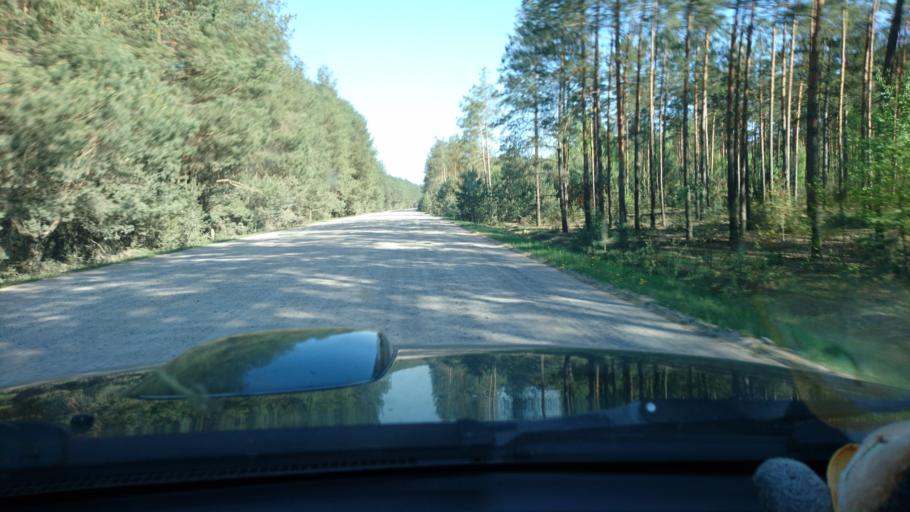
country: BY
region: Brest
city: Zhabinka
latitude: 52.3879
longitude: 24.1044
